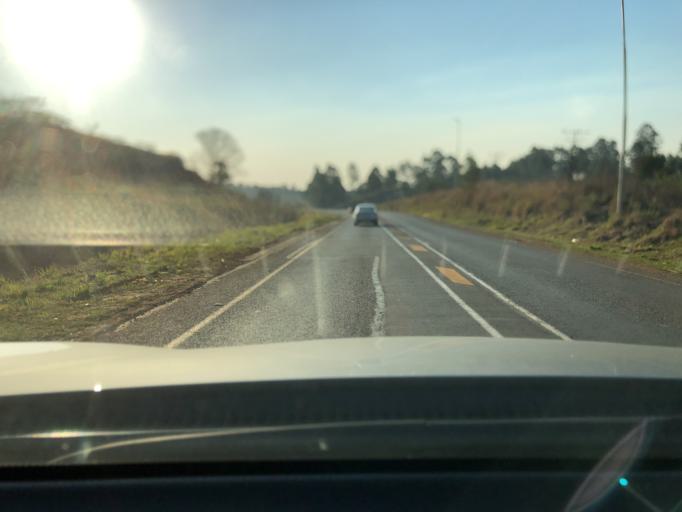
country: ZA
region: KwaZulu-Natal
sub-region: Sisonke District Municipality
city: Ixopo
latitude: -30.1556
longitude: 30.0792
